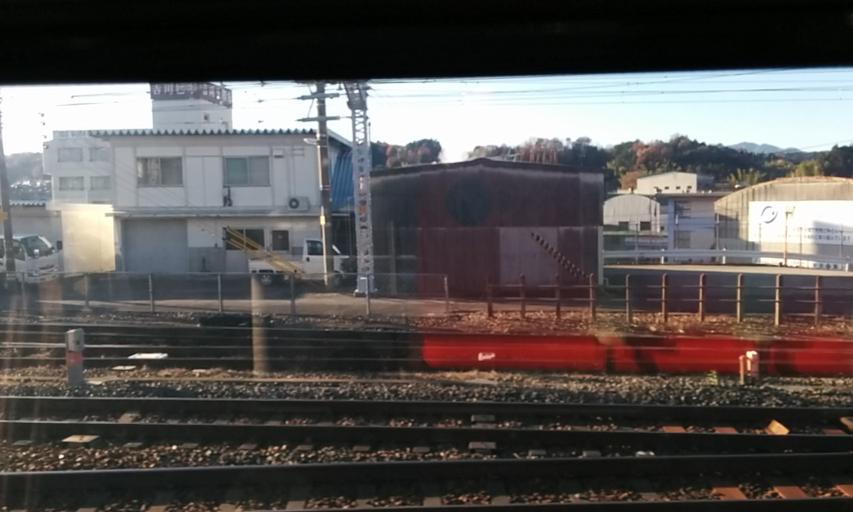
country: JP
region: Gifu
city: Nakatsugawa
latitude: 35.5017
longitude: 137.5033
